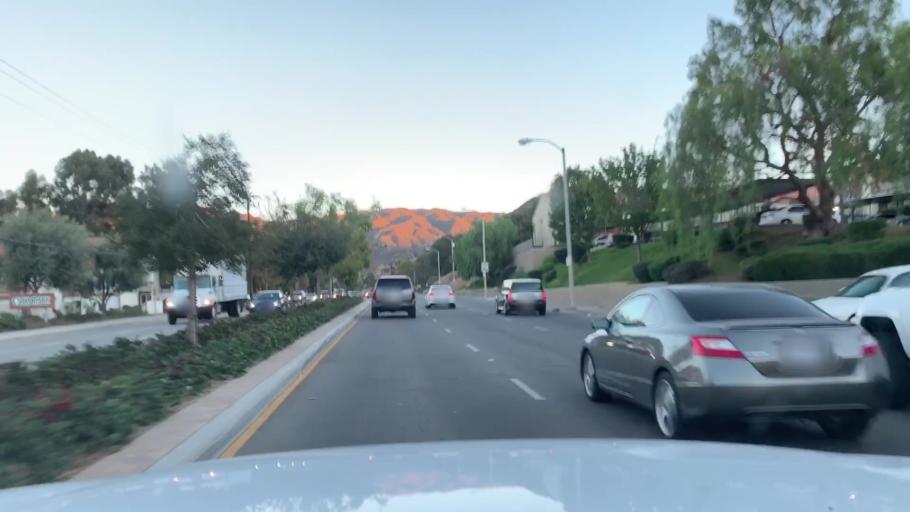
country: US
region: California
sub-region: Los Angeles County
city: Santa Clarita
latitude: 34.3691
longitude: -118.5122
